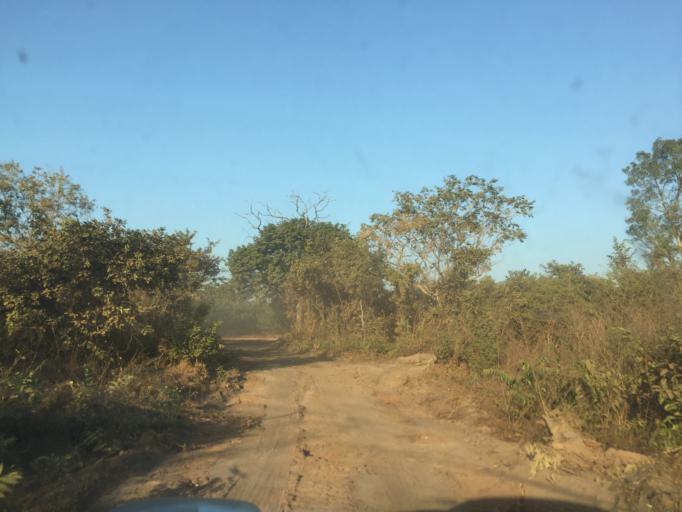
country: GW
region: Oio
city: Farim
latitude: 12.5311
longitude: -15.2753
